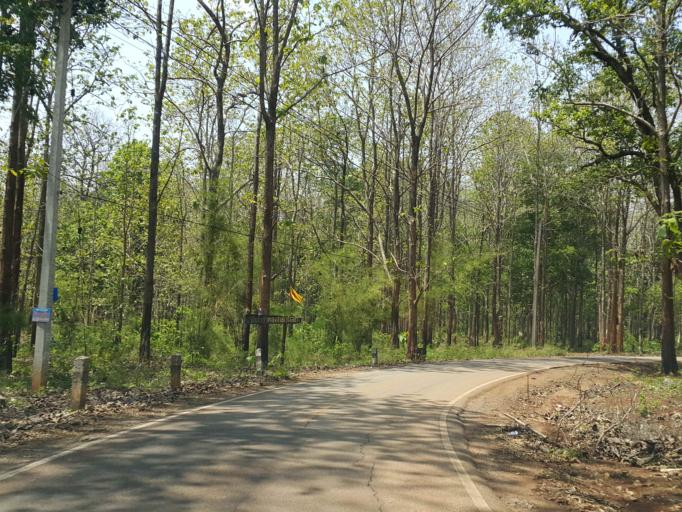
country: TH
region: Chiang Mai
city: Mae Taeng
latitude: 19.0756
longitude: 99.0868
